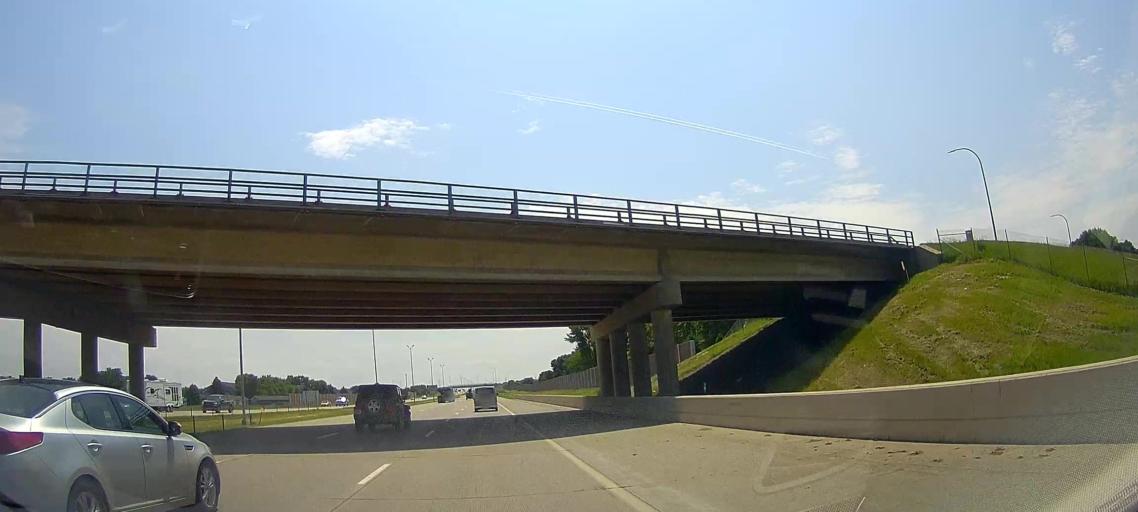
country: US
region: South Dakota
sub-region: Lincoln County
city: Tea
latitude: 43.5075
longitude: -96.7836
